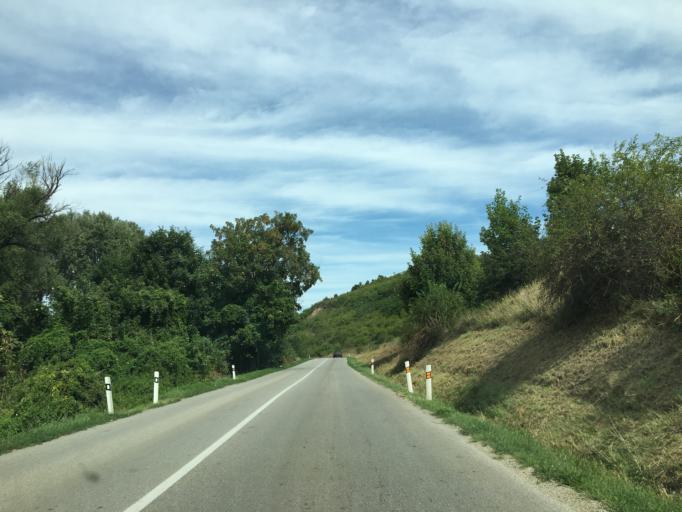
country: SK
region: Nitriansky
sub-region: Okres Nove Zamky
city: Sturovo
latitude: 47.8358
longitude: 18.7230
